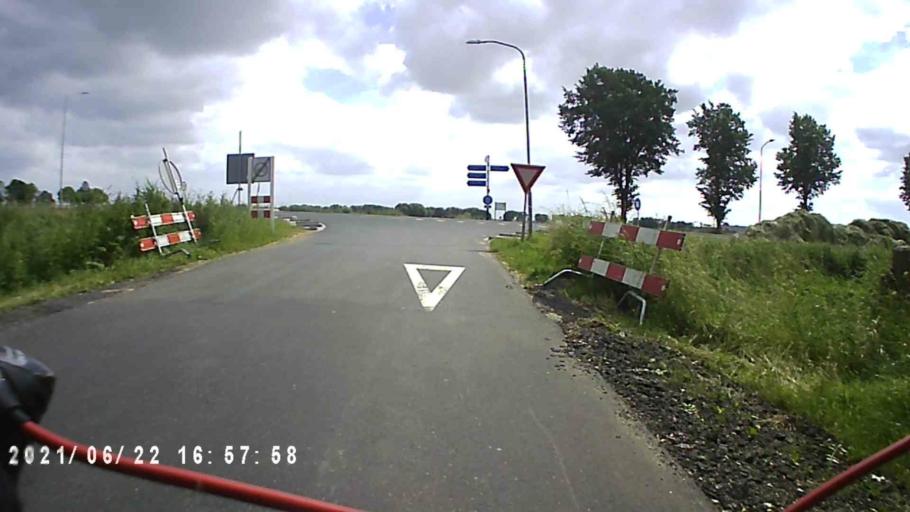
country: NL
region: Groningen
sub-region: Gemeente Bedum
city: Bedum
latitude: 53.3027
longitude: 6.6471
